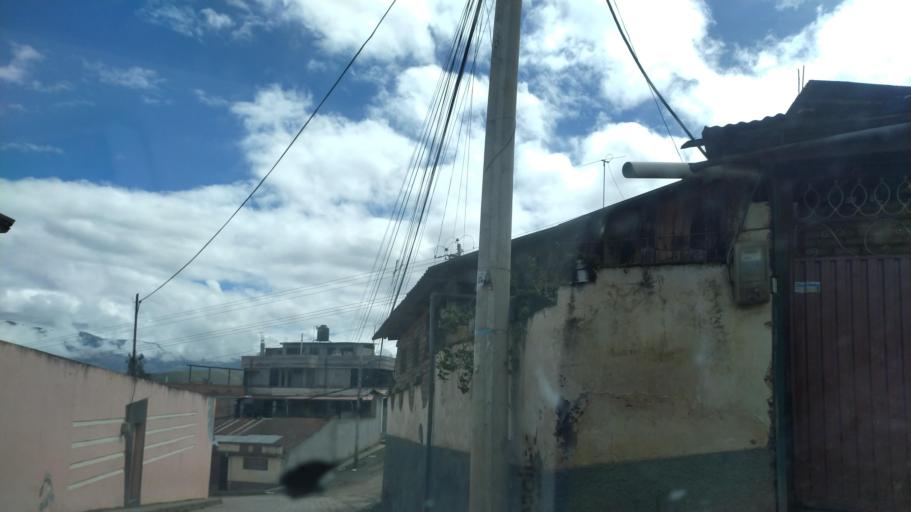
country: EC
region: Chimborazo
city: Riobamba
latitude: -1.6585
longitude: -78.5665
